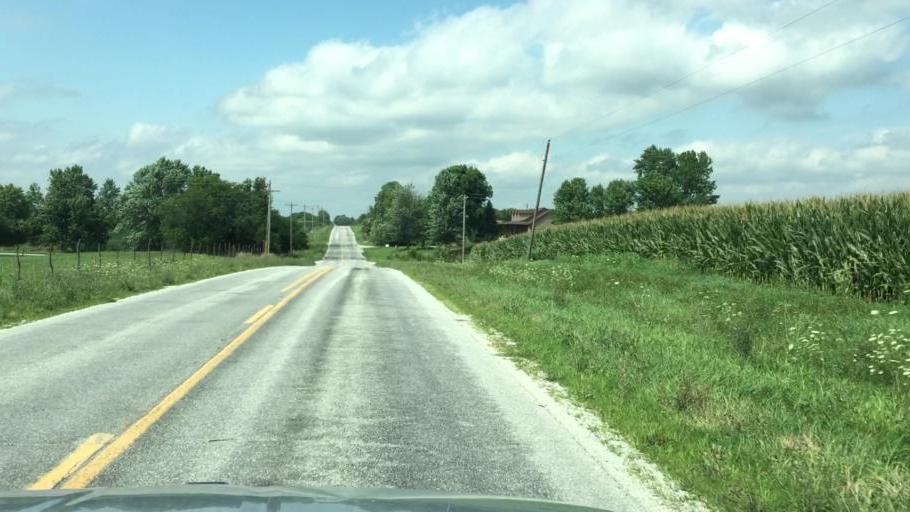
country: US
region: Illinois
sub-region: Hancock County
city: Nauvoo
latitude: 40.5208
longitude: -91.3078
